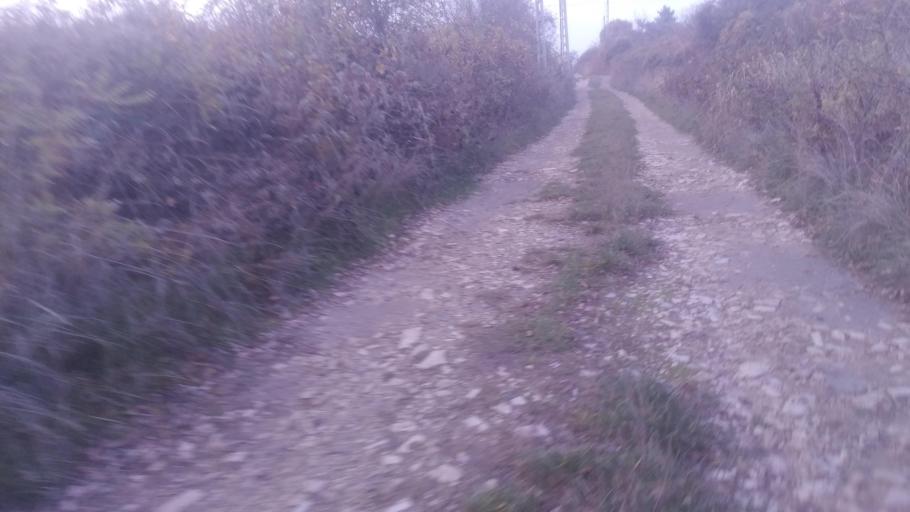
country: HU
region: Pest
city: Urom
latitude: 47.6016
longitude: 19.0279
